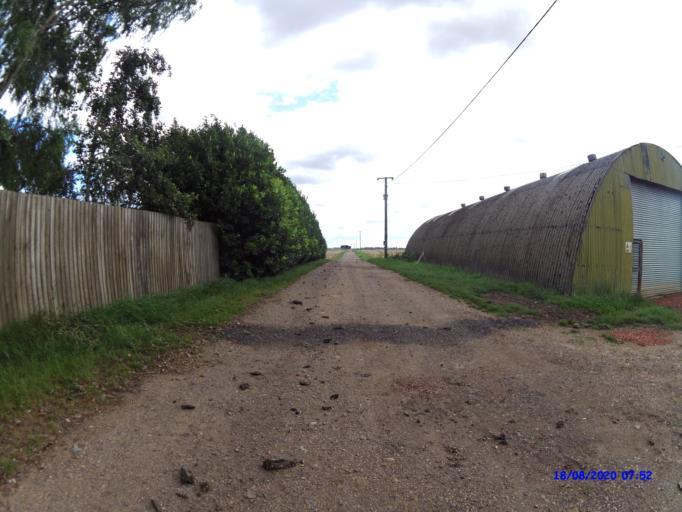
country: GB
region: England
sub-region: Cambridgeshire
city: Whittlesey
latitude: 52.5182
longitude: -0.0912
